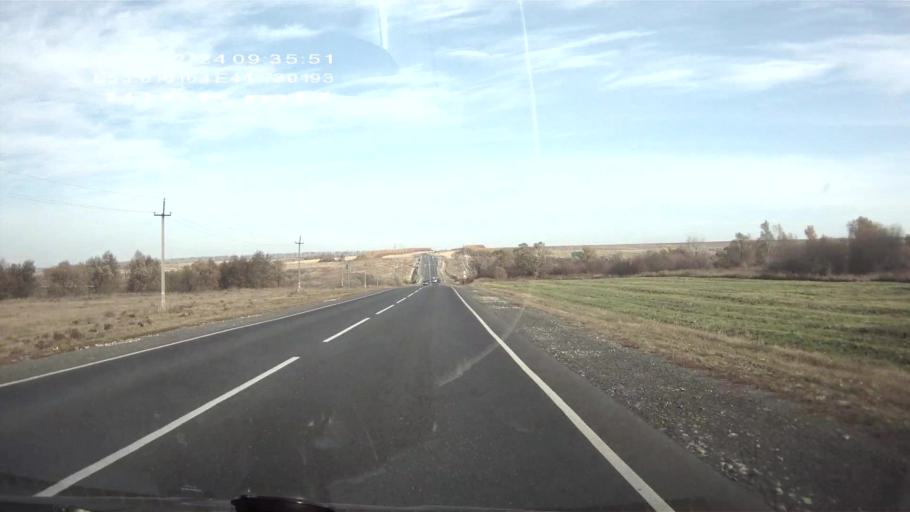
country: RU
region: Penza
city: Mokshan
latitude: 53.6102
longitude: 44.7303
